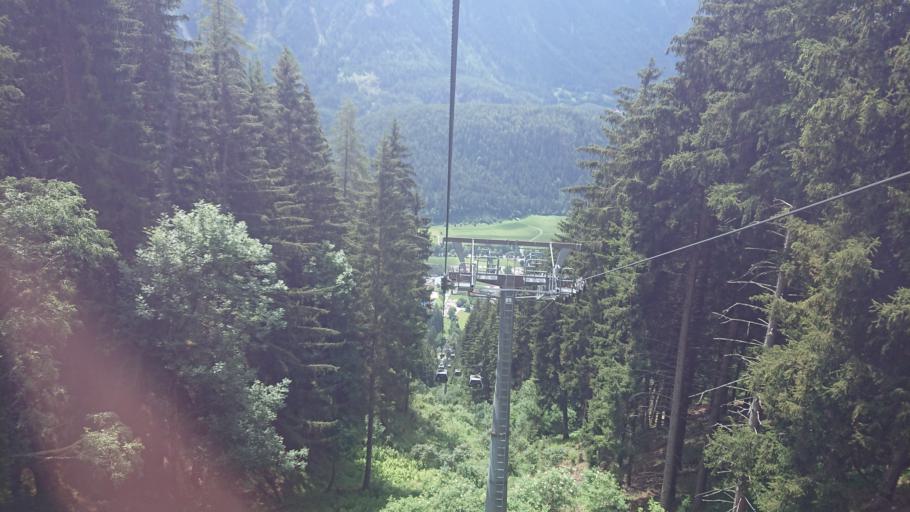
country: AT
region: Tyrol
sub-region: Politischer Bezirk Imst
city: Oetz
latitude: 47.2048
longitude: 10.9148
